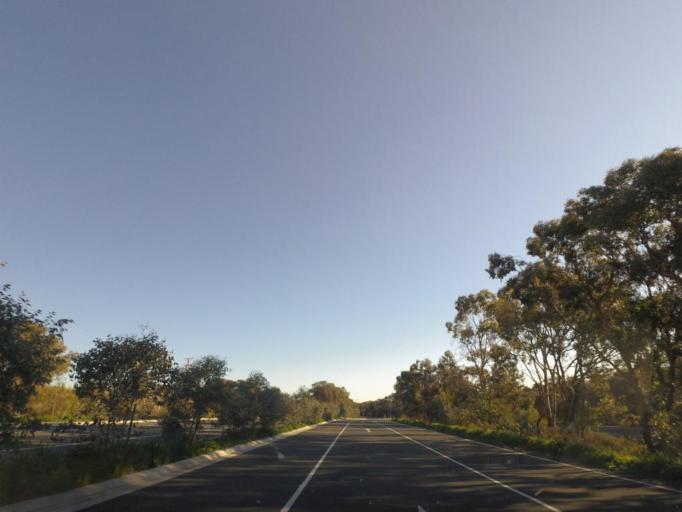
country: AU
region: Victoria
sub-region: Greater Shepparton
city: Shepparton
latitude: -36.7813
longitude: 145.5011
